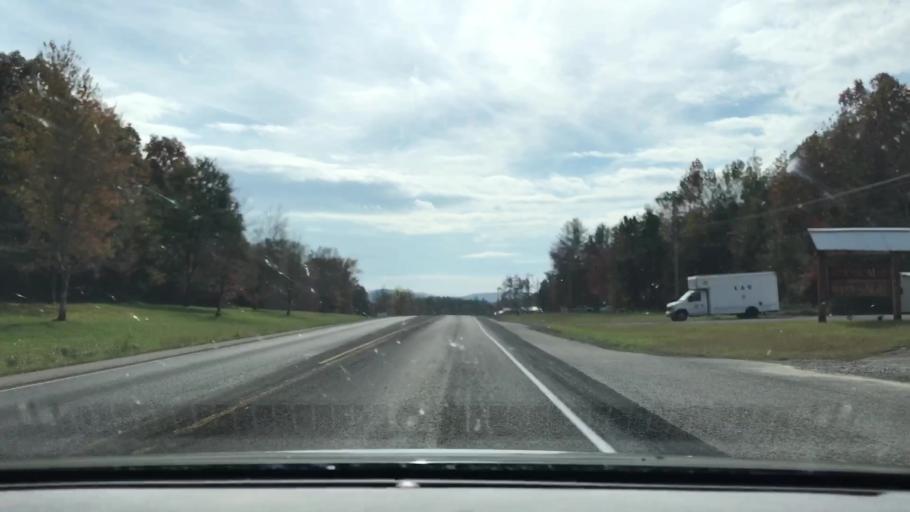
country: US
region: Kentucky
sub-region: McCreary County
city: Pine Knot
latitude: 36.5875
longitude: -84.4391
